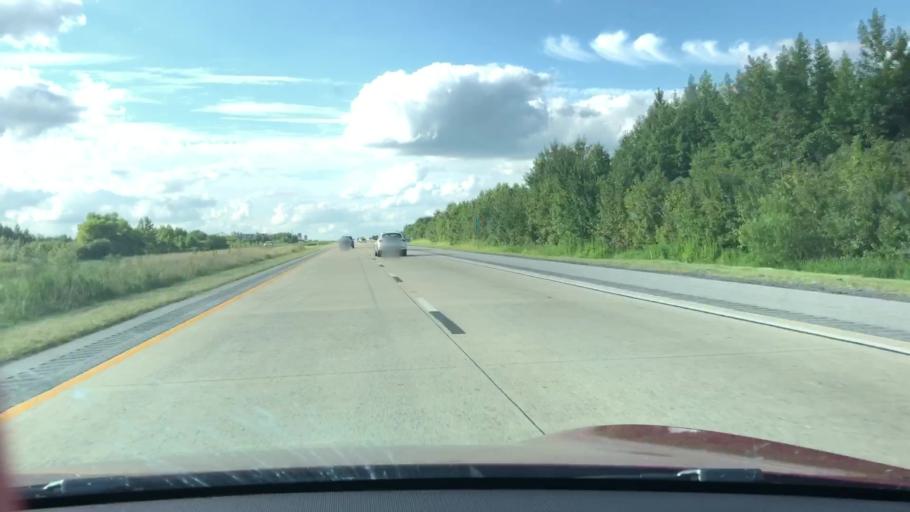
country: US
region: Delaware
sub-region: New Castle County
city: Townsend
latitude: 39.3796
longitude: -75.6602
